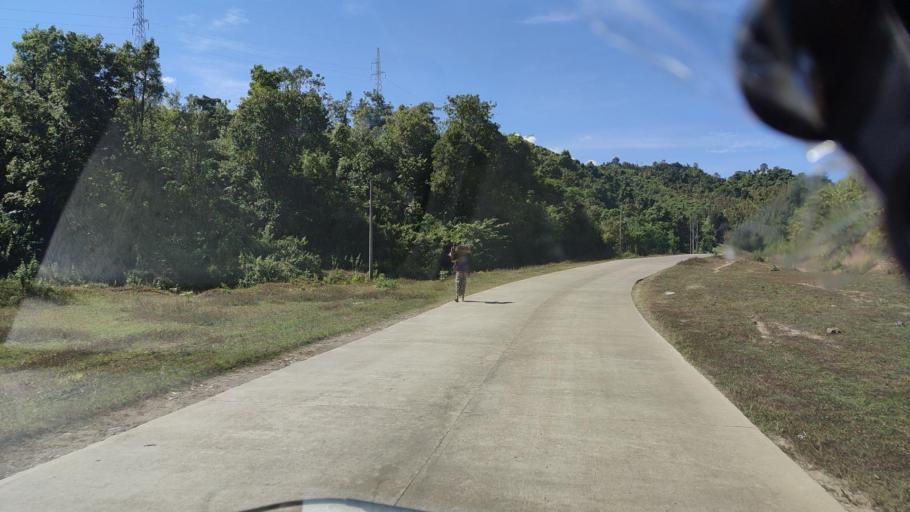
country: MM
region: Rakhine
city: Sittwe
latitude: 20.2249
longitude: 93.4041
